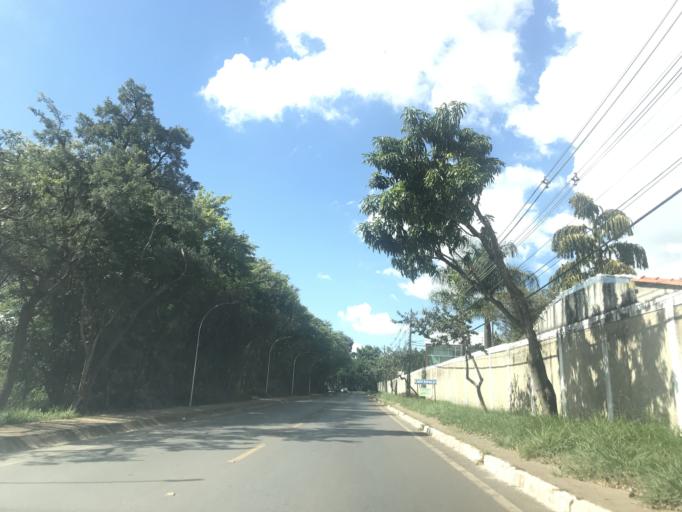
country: BR
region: Federal District
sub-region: Brasilia
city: Brasilia
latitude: -15.8805
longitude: -47.8092
